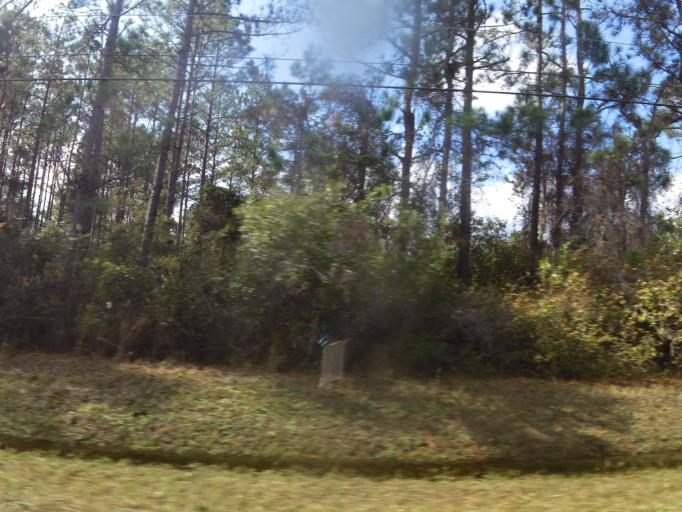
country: US
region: Florida
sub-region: Duval County
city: Baldwin
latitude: 30.1912
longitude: -81.9911
